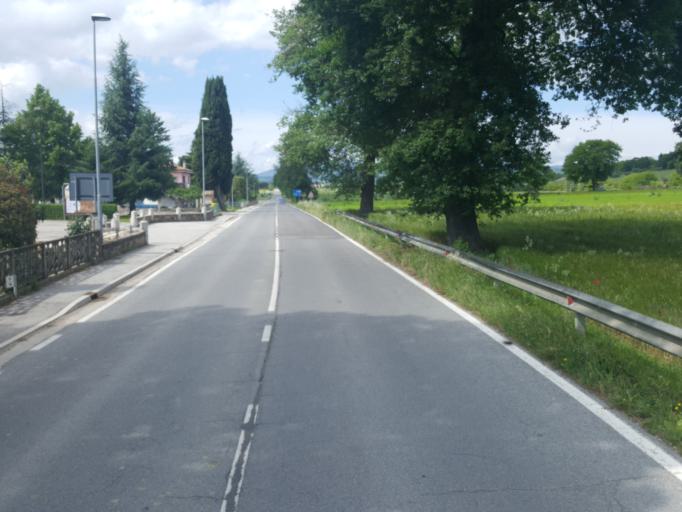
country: IT
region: The Marches
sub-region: Provincia di Macerata
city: Casette Verdini
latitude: 43.2404
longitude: 13.3697
